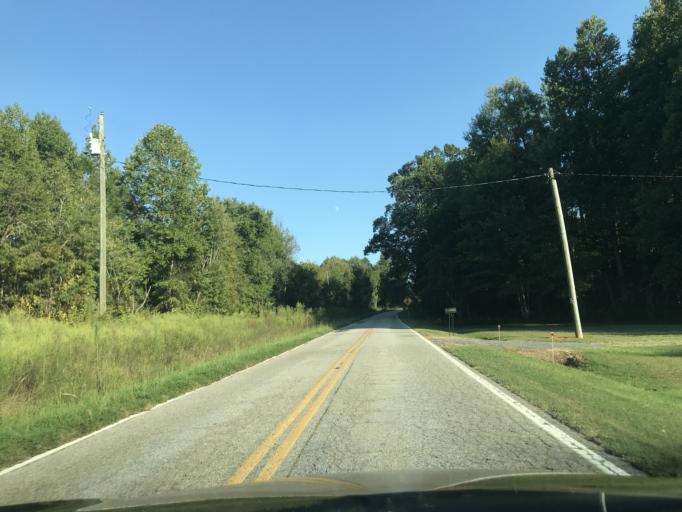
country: US
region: South Carolina
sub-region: Spartanburg County
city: Mayo
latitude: 35.1182
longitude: -81.7863
